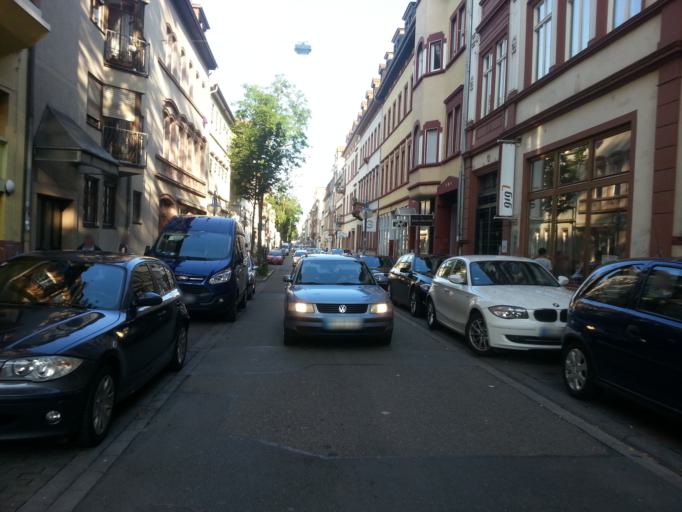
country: DE
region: Rheinland-Pfalz
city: Ludwigshafen am Rhein
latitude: 49.4929
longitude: 8.4607
